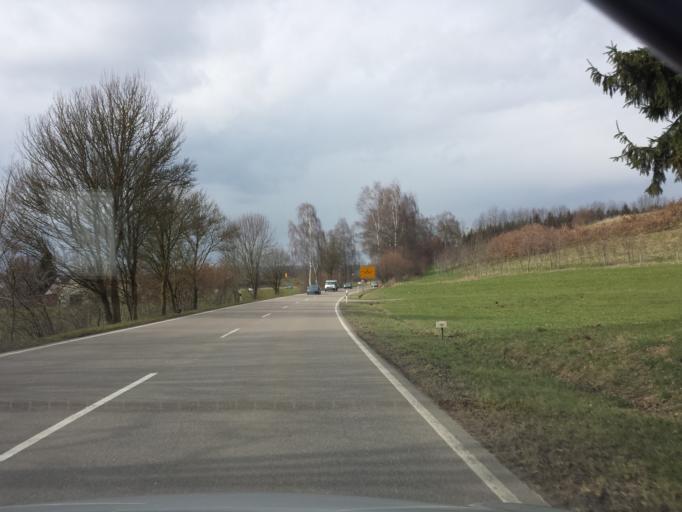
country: DE
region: Baden-Wuerttemberg
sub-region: Tuebingen Region
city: Achstetten
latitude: 48.2568
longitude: 9.9100
